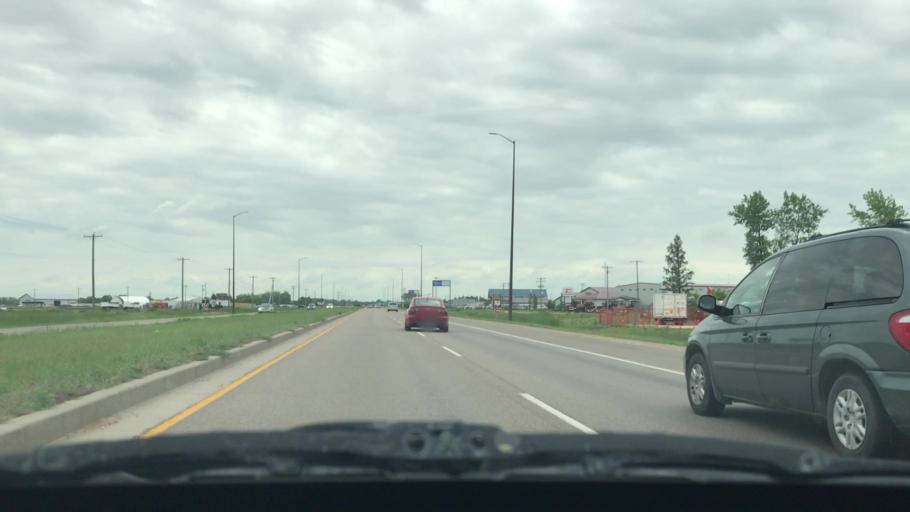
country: CA
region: Manitoba
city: Winnipeg
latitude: 49.8501
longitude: -97.0011
